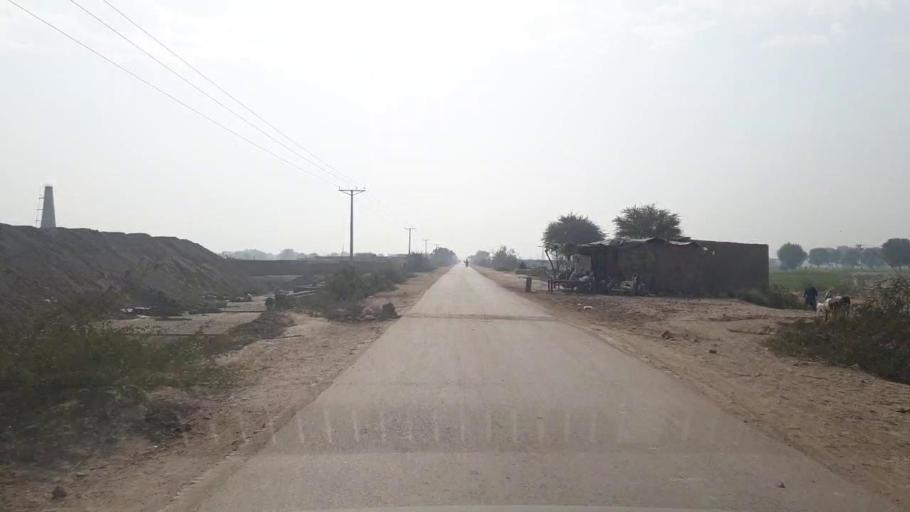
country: PK
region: Sindh
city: Hala
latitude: 25.7751
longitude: 68.4447
